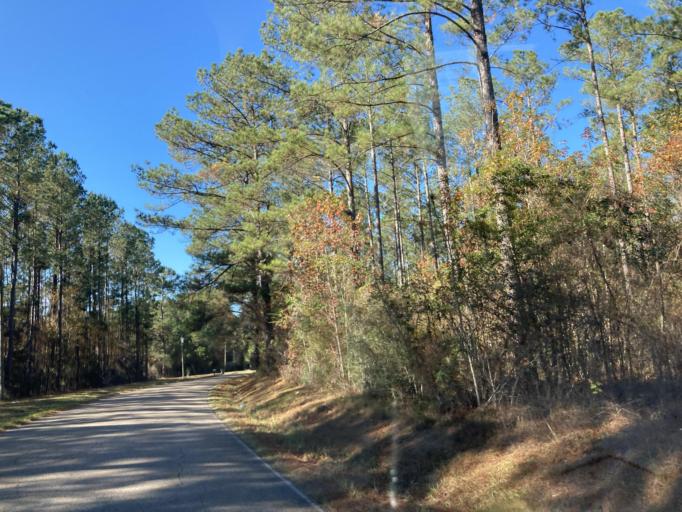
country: US
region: Mississippi
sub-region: Lamar County
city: Sumrall
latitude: 31.3094
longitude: -89.6109
